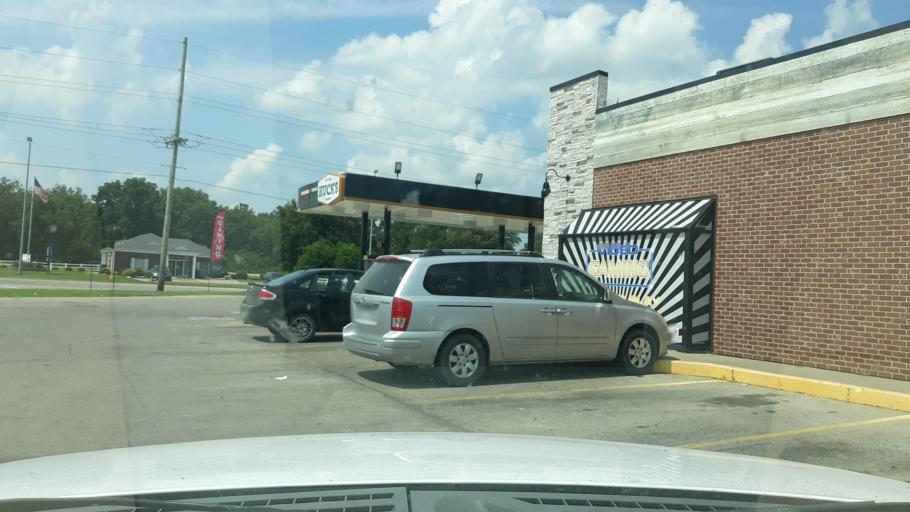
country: US
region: Illinois
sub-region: Saline County
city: Eldorado
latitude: 37.8068
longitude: -88.4395
